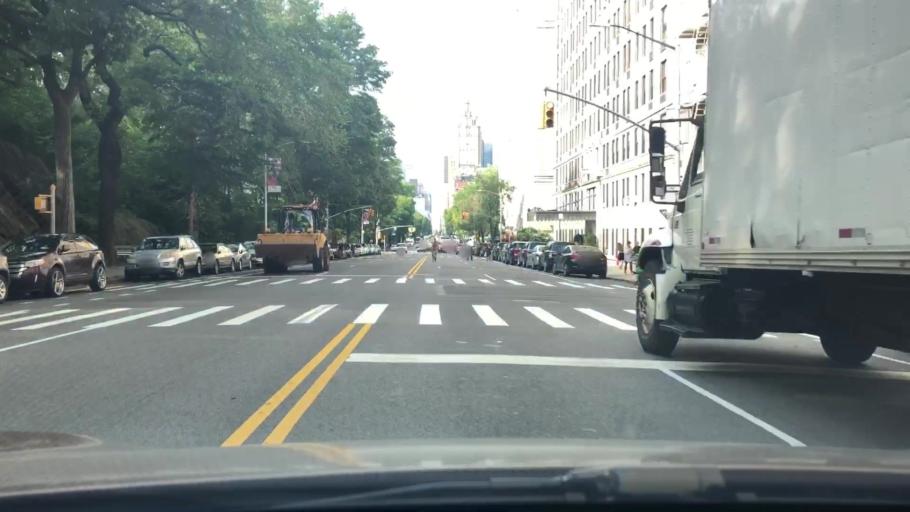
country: US
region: New York
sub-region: New York County
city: Manhattan
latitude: 40.7835
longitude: -73.9707
